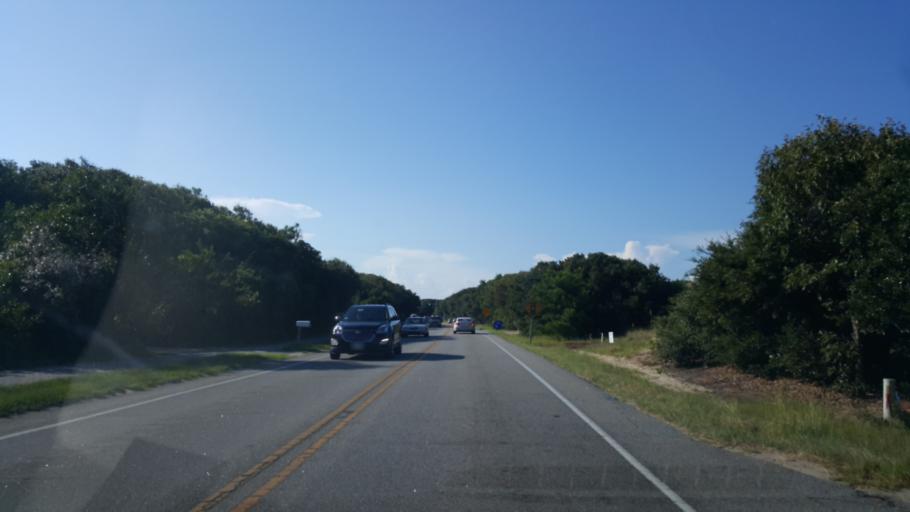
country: US
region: North Carolina
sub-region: Dare County
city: Southern Shores
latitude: 36.1266
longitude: -75.7283
